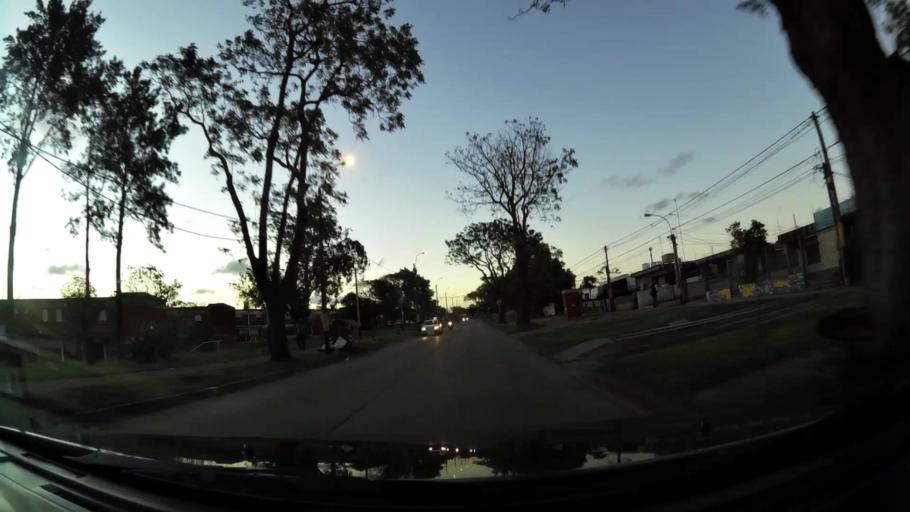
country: UY
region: Canelones
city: Paso de Carrasco
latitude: -34.8747
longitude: -56.0928
